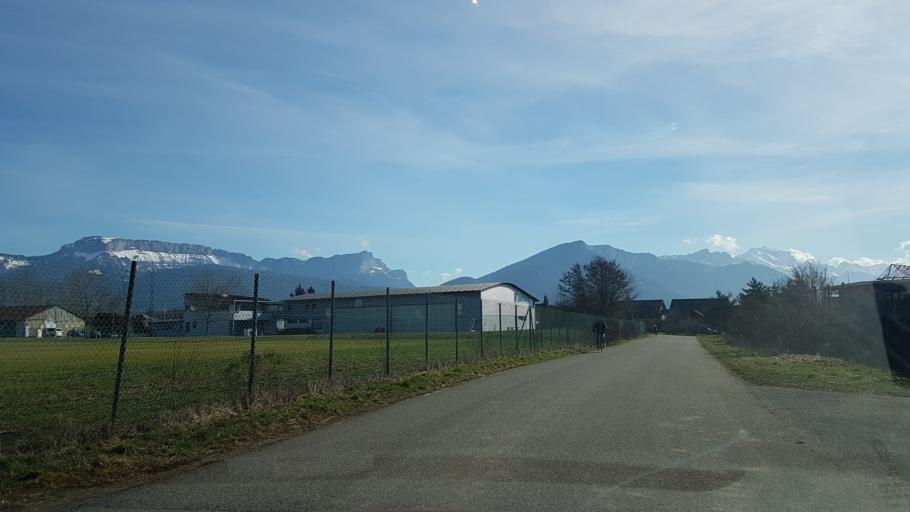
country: FR
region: Rhone-Alpes
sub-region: Departement de la Haute-Savoie
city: Metz-Tessy
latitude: 45.9269
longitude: 6.1017
